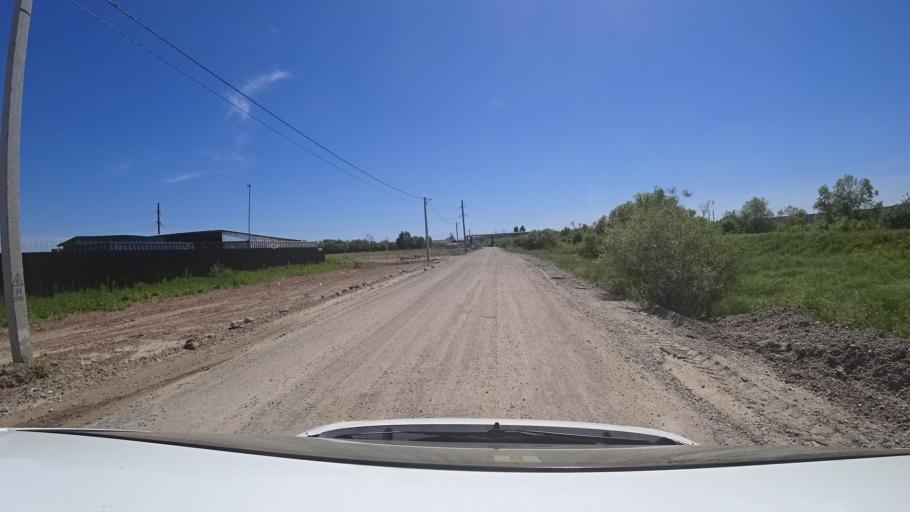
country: RU
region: Khabarovsk Krai
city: Topolevo
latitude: 48.4767
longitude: 135.1720
